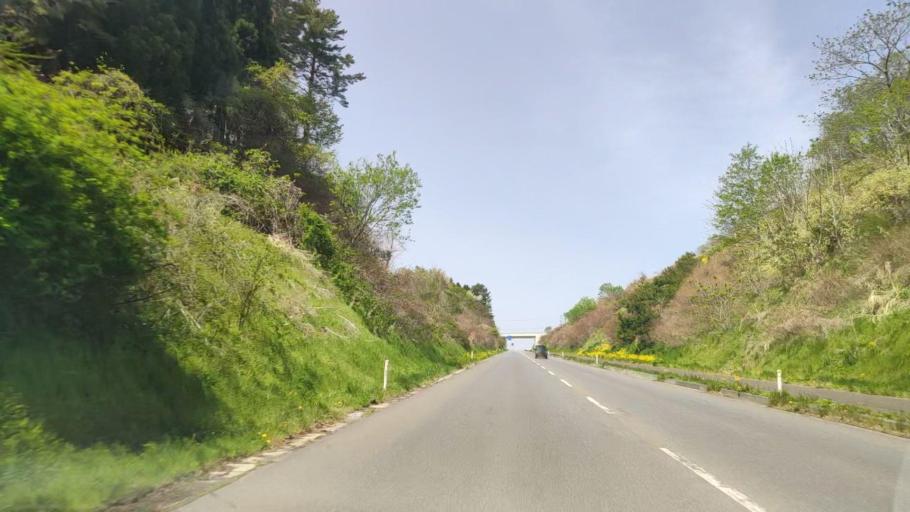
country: JP
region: Aomori
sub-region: Hachinohe Shi
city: Uchimaru
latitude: 40.5242
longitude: 141.4140
